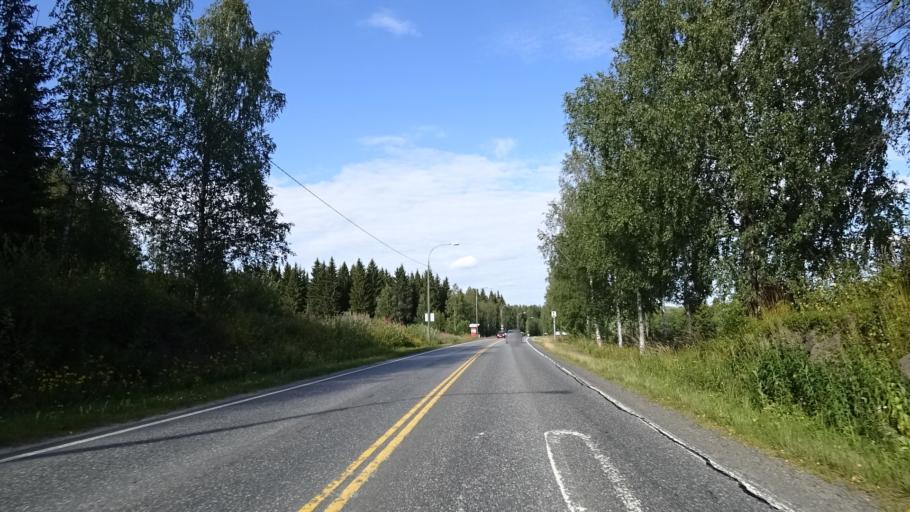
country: FI
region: North Karelia
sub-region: Joensuu
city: Eno
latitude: 62.7893
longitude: 30.0820
